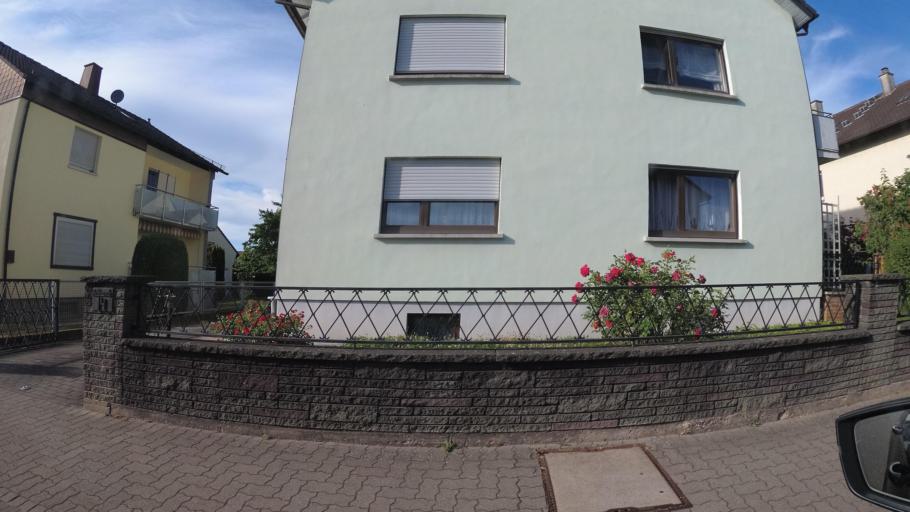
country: DE
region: Baden-Wuerttemberg
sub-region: Karlsruhe Region
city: Weingarten
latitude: 49.0672
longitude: 8.4685
